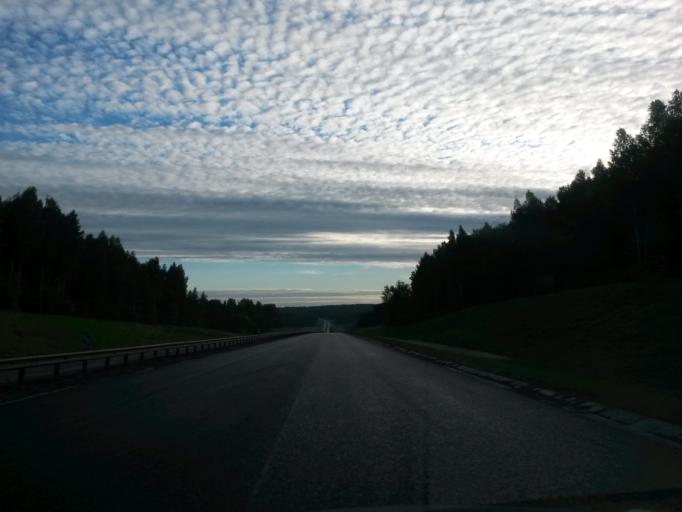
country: RU
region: Vladimir
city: Strunino
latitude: 56.5271
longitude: 38.5701
